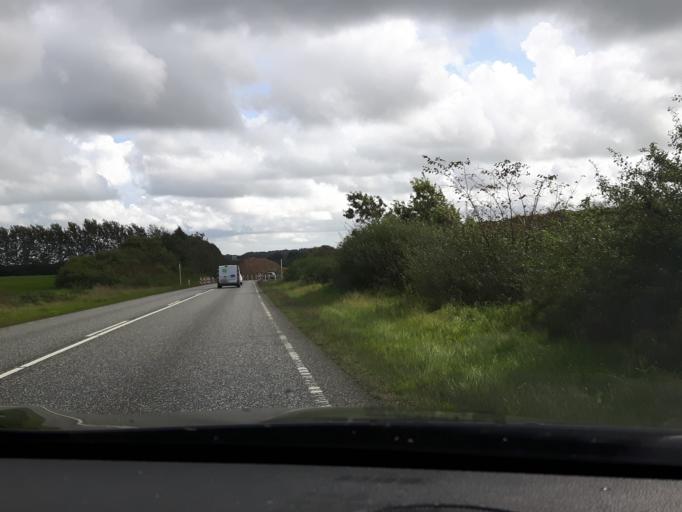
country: DK
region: Central Jutland
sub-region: Herning Kommune
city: Avlum
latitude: 56.2439
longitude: 8.8015
